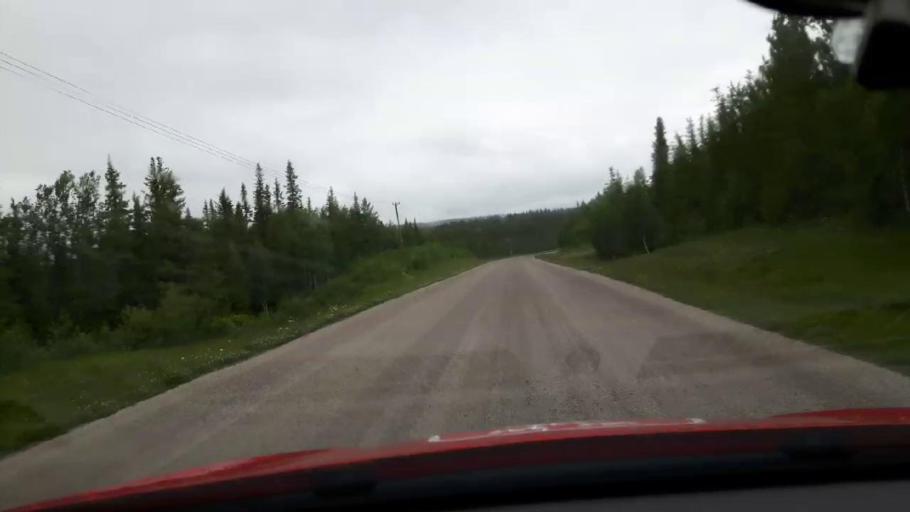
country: NO
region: Nord-Trondelag
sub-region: Meraker
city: Meraker
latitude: 63.2776
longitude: 12.3576
